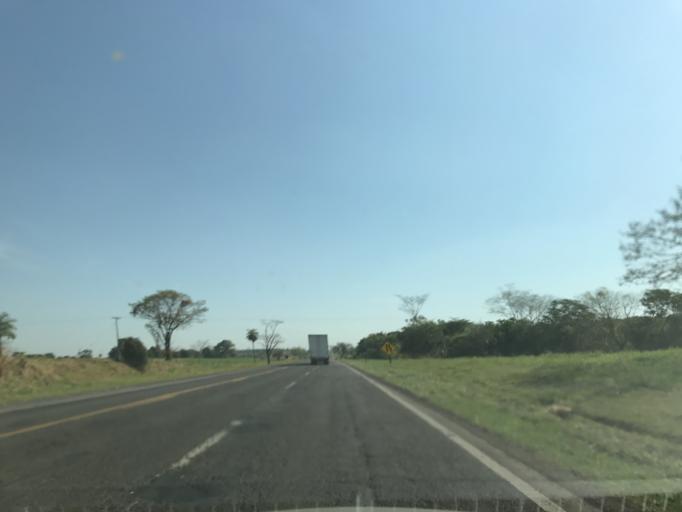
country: BR
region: Sao Paulo
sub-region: Penapolis
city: Penapolis
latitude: -21.4623
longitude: -50.1768
